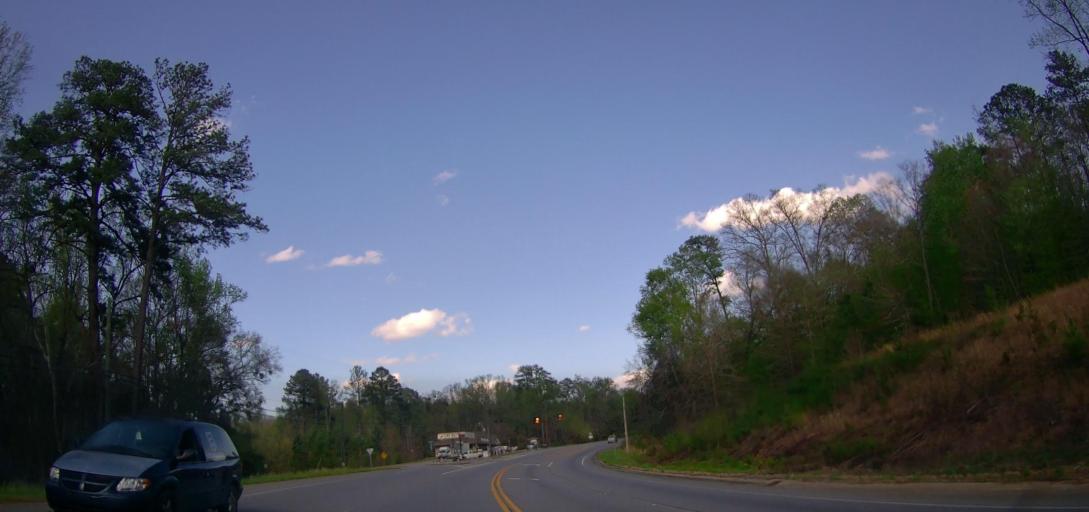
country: US
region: Georgia
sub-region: Baldwin County
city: Hardwick
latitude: 33.0887
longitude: -83.1968
